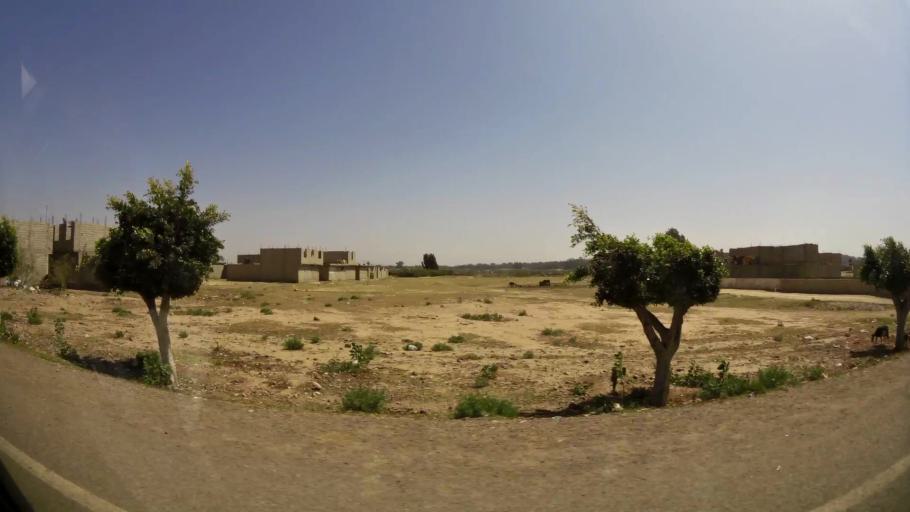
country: MA
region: Souss-Massa-Draa
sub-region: Inezgane-Ait Mellou
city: Inezgane
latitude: 30.3442
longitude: -9.5506
